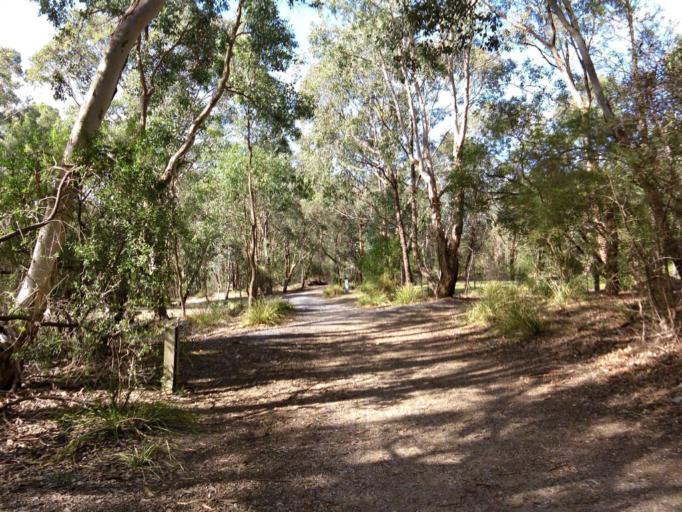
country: AU
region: Victoria
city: Mitcham
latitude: -37.8069
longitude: 145.2038
